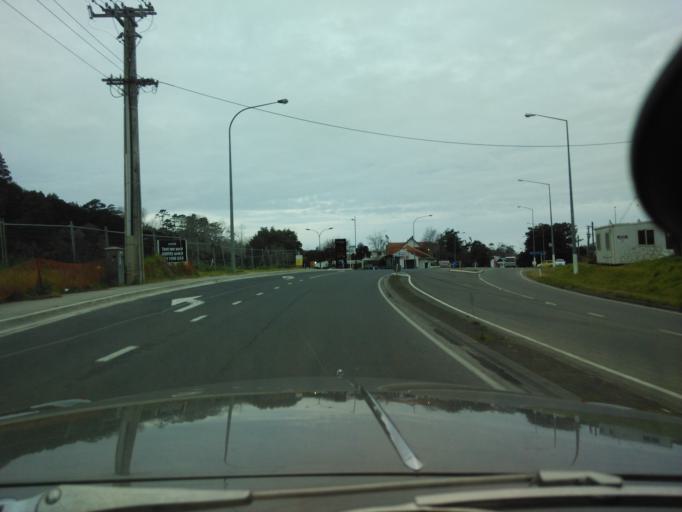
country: NZ
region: Auckland
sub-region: Auckland
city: Rothesay Bay
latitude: -36.7215
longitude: 174.6904
